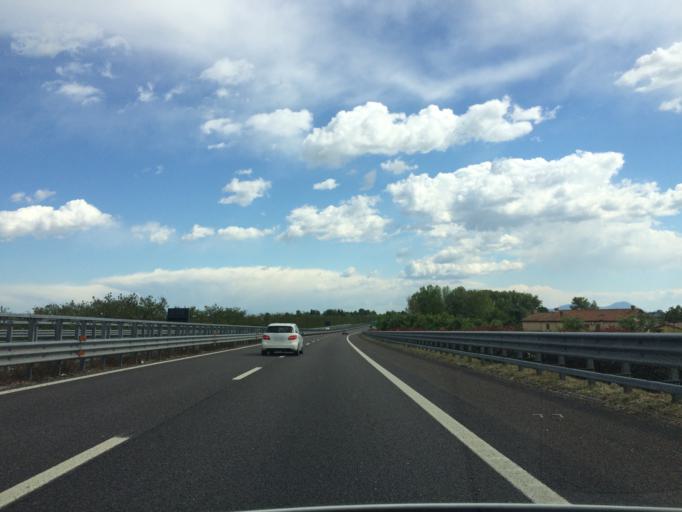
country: IT
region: Veneto
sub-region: Provincia di Vicenza
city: Lisiera
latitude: 45.5726
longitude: 11.6077
